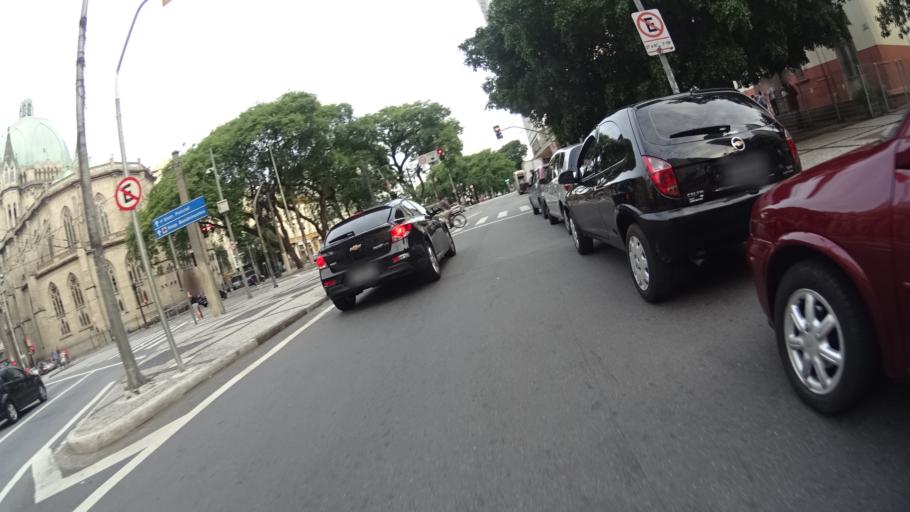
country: BR
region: Sao Paulo
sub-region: Sao Paulo
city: Sao Paulo
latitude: -23.5521
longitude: -46.6355
